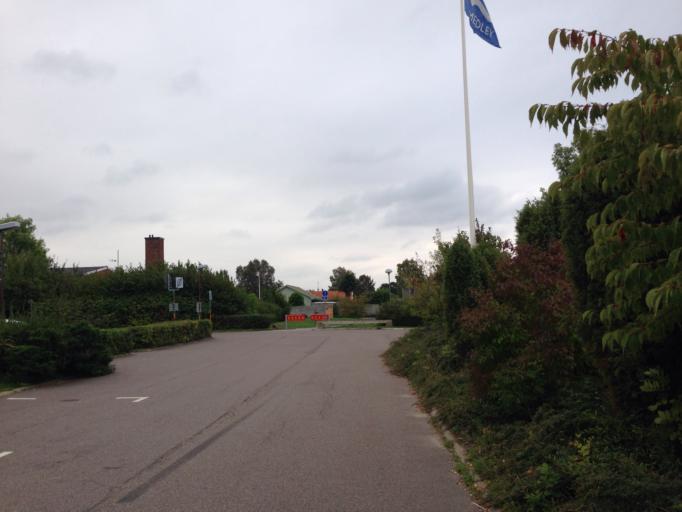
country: SE
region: Skane
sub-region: Lomma Kommun
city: Lomma
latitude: 55.6707
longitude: 13.0816
